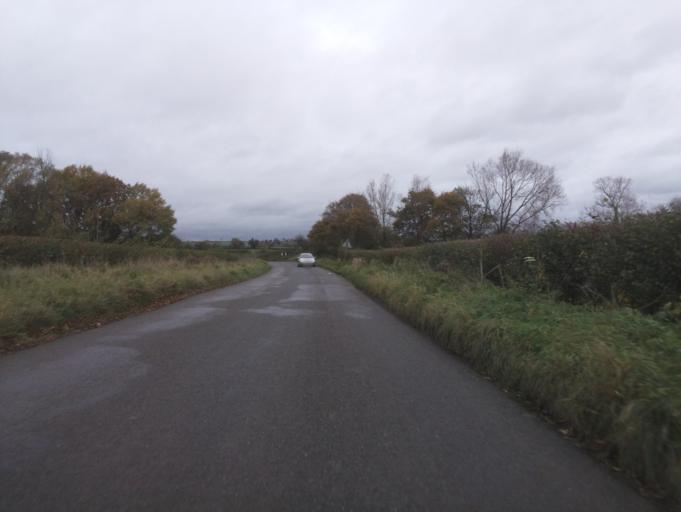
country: GB
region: England
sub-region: Somerset
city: Yeovil
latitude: 51.0064
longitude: -2.5945
